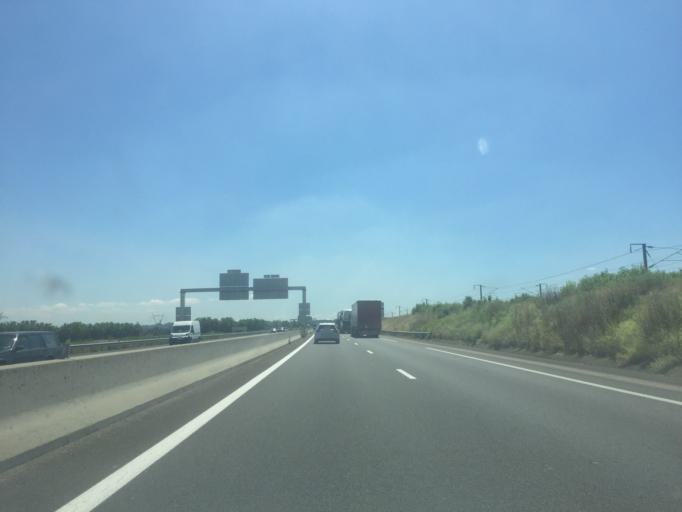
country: FR
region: Rhone-Alpes
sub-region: Departement de l'Ain
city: Thil
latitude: 45.8217
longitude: 5.0399
